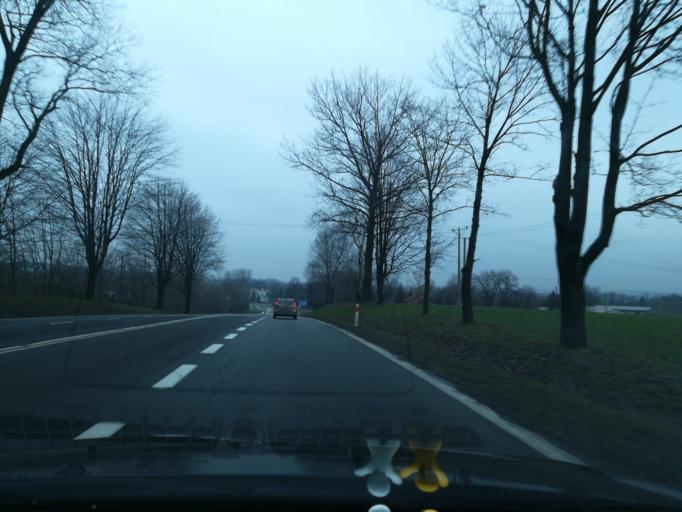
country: PL
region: Subcarpathian Voivodeship
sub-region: Powiat lancucki
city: Gluchow
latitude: 50.0805
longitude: 22.2775
